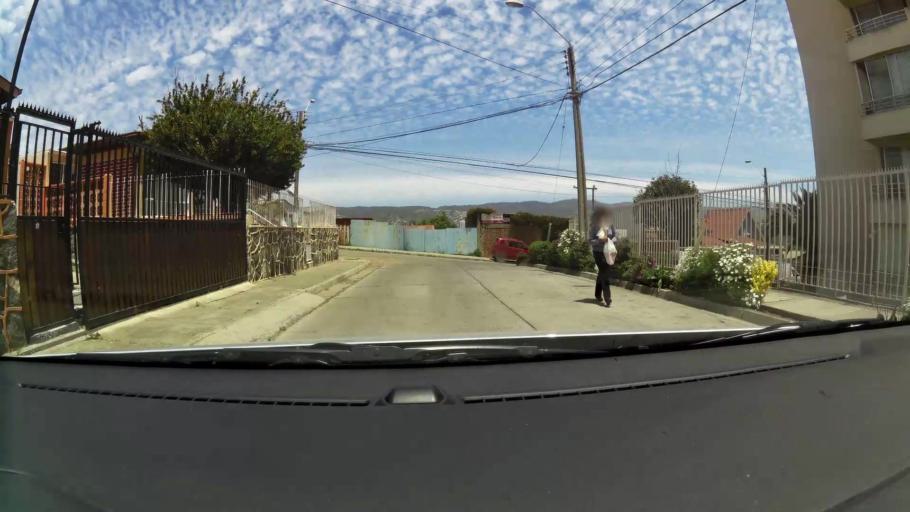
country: CL
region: Valparaiso
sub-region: Provincia de Valparaiso
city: Vina del Mar
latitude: -33.0489
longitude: -71.5799
